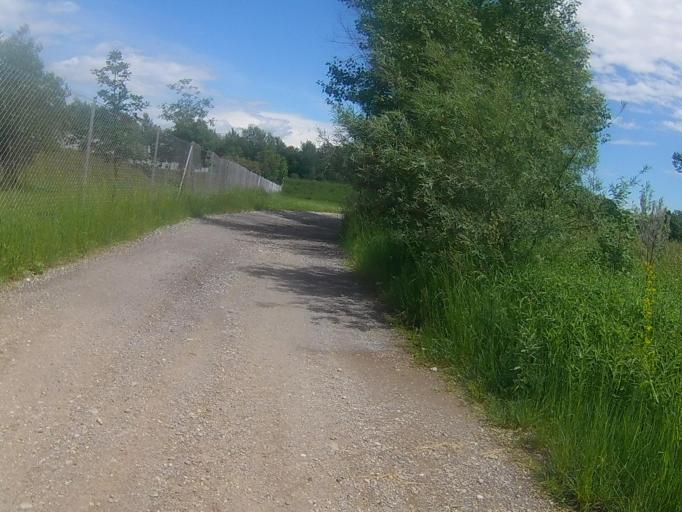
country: SI
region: Duplek
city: Zgornji Duplek
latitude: 46.5087
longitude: 15.7136
